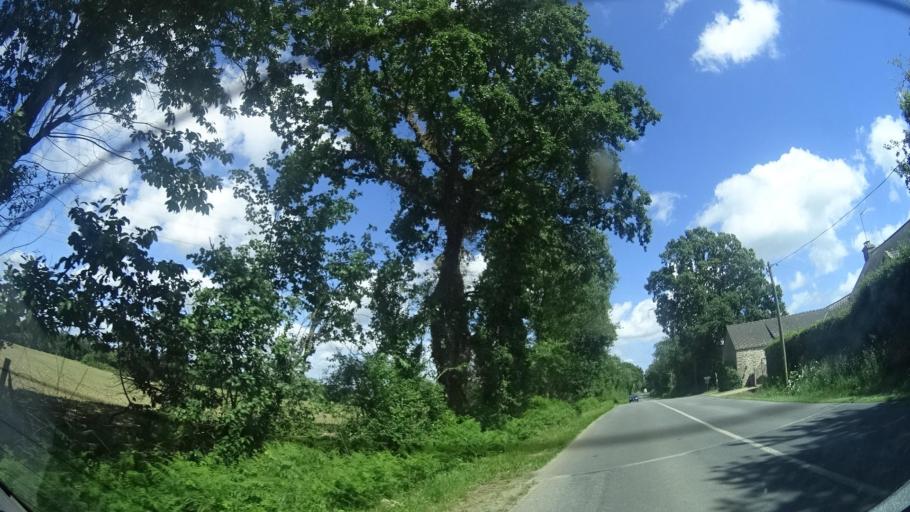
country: FR
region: Brittany
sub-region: Departement du Morbihan
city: Pluherlin
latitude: 47.6780
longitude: -2.3853
